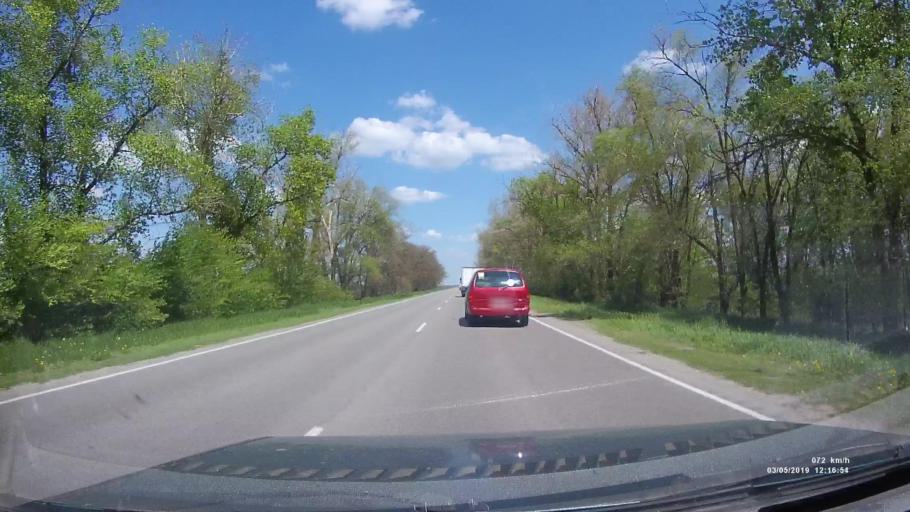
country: RU
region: Rostov
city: Melikhovskaya
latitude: 47.3775
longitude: 40.5884
